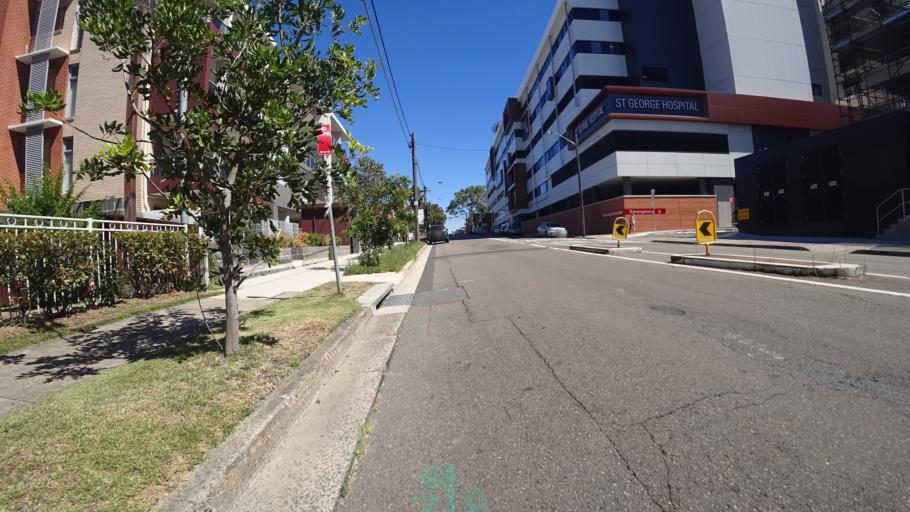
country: AU
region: New South Wales
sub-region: Kogarah
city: Beverly Park
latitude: -33.9681
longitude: 151.1332
